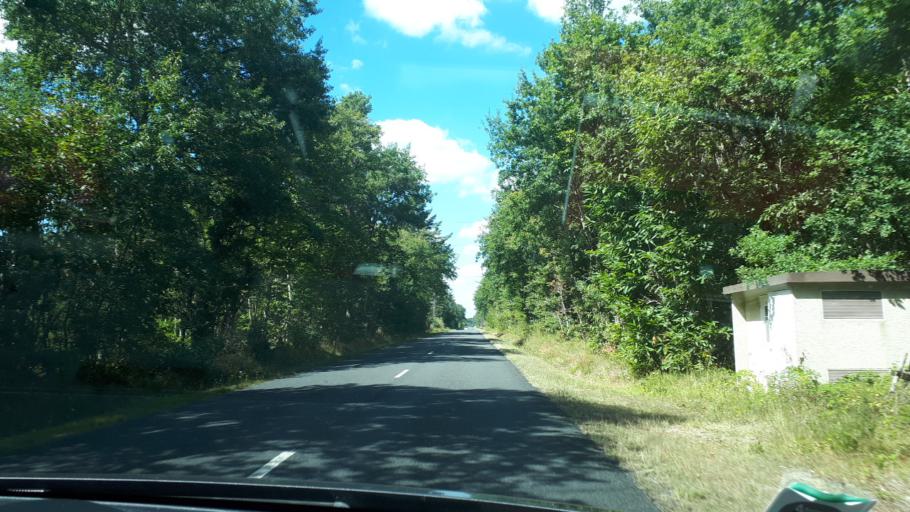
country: FR
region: Centre
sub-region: Departement du Loir-et-Cher
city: Dhuizon
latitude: 47.5344
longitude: 1.7093
